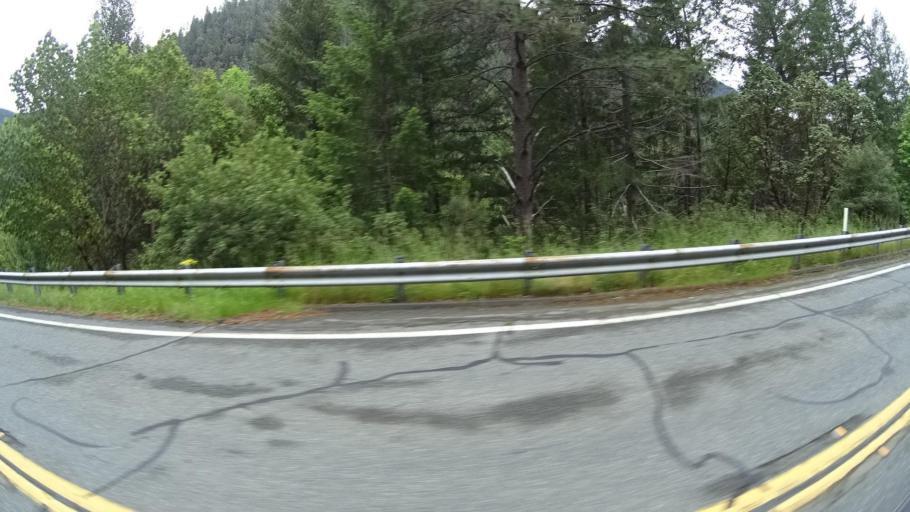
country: US
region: California
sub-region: Humboldt County
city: Willow Creek
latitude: 41.2600
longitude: -123.6124
